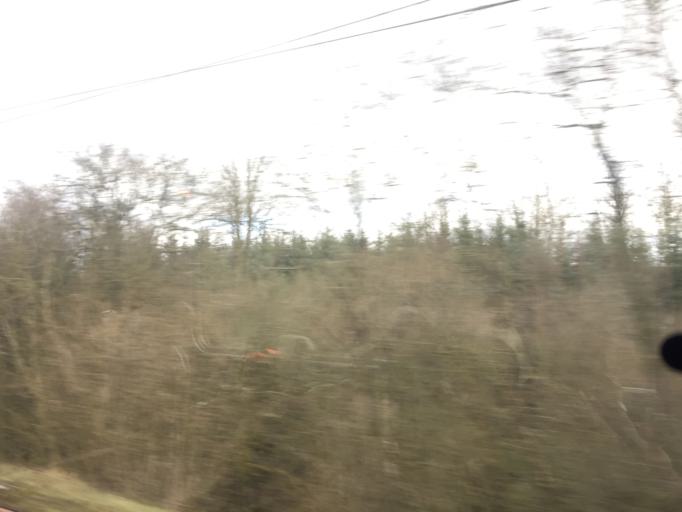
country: GB
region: Scotland
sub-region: Dumfries and Galloway
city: Lochmaben
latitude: 55.1778
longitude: -3.3978
